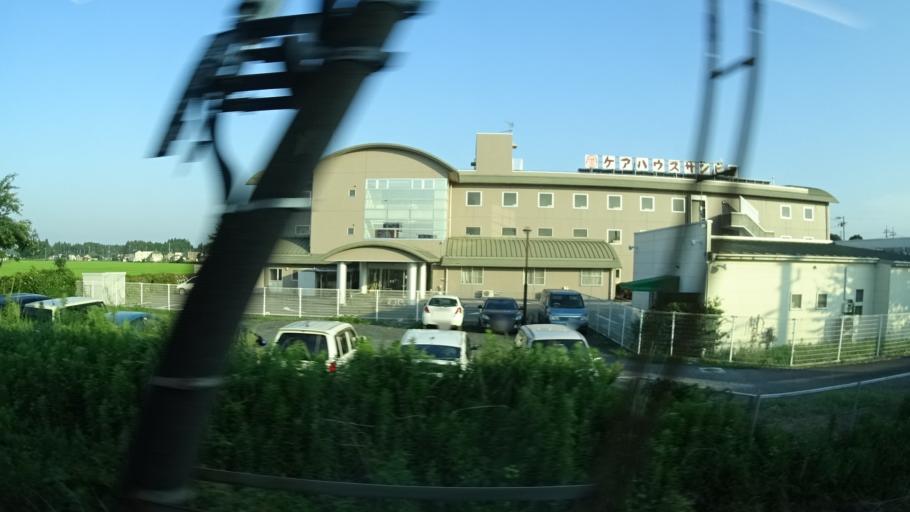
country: JP
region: Ibaraki
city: Tomobe
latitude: 36.3718
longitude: 140.3565
